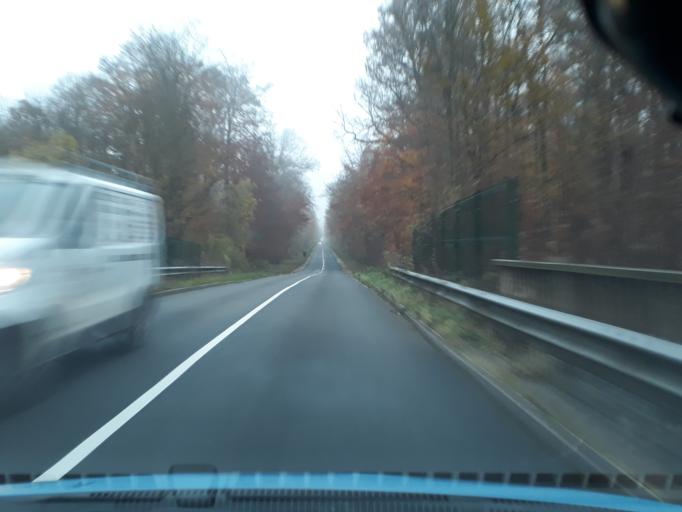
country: FR
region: Ile-de-France
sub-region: Departement de Seine-et-Marne
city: Thomery
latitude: 48.3940
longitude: 2.7688
